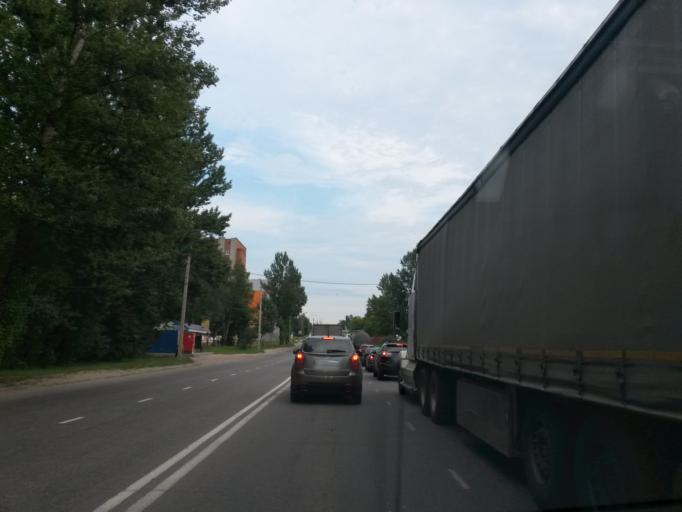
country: RU
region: Jaroslavl
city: Yaroslavl
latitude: 57.5782
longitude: 39.8376
